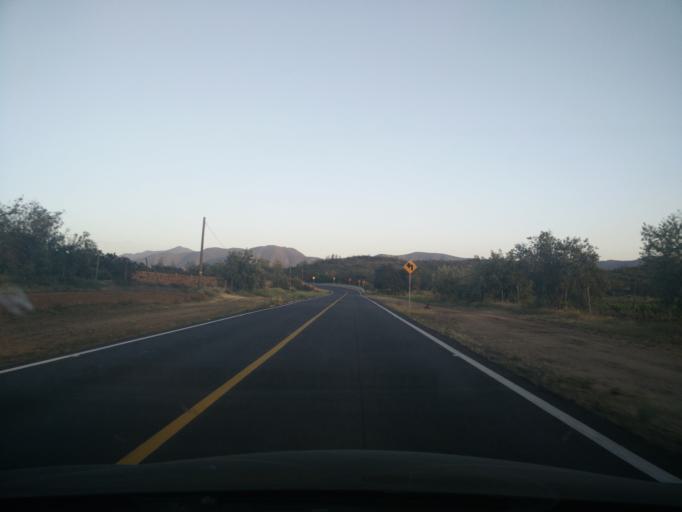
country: MX
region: Baja California
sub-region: Ensenada
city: Rancho Verde
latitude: 31.9946
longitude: -116.6551
